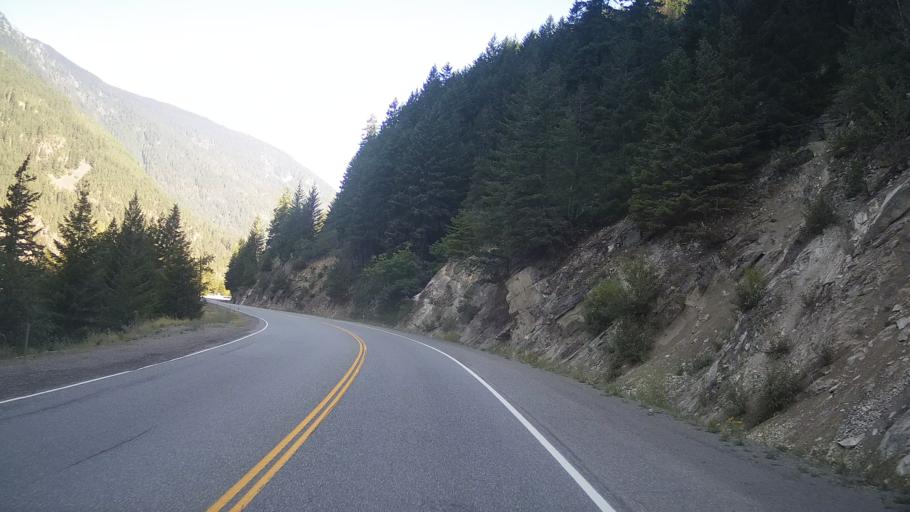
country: CA
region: British Columbia
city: Hope
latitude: 49.7731
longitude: -121.4368
